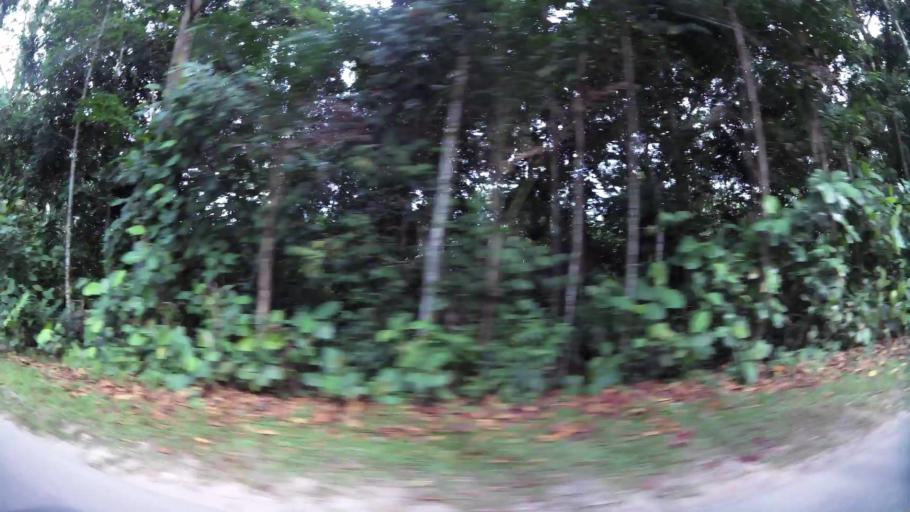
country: MY
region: Johor
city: Johor Bahru
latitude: 1.4132
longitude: 103.6997
